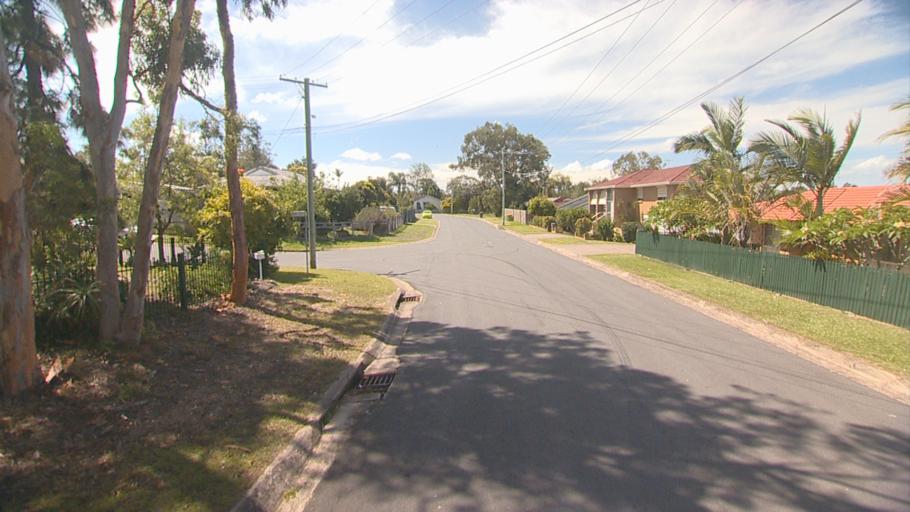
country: AU
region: Queensland
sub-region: Logan
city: Beenleigh
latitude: -27.7060
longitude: 153.2076
